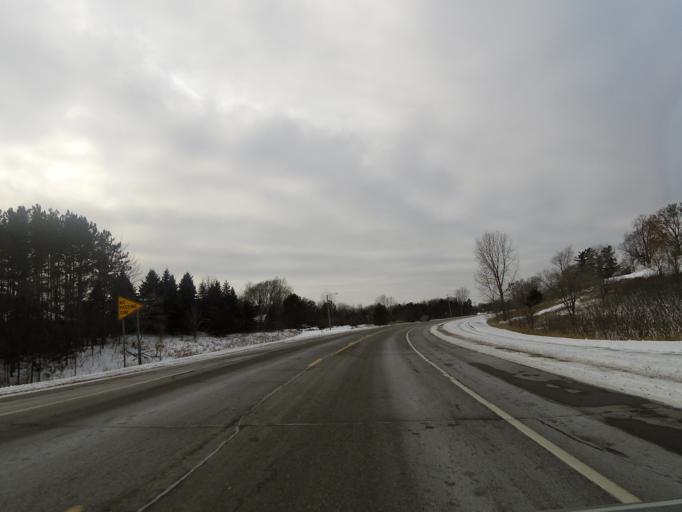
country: US
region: Minnesota
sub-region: Washington County
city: Woodbury
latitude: 44.8902
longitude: -92.9134
